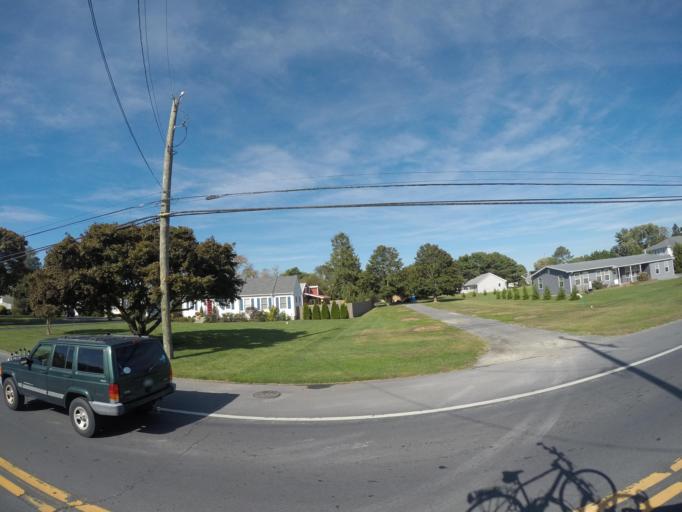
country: US
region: Delaware
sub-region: Sussex County
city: Lewes
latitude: 38.7561
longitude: -75.1587
